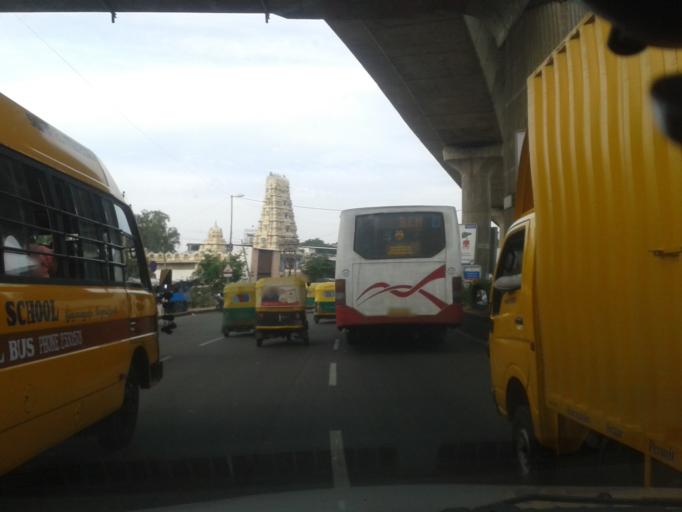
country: IN
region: Karnataka
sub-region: Bangalore Urban
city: Bangalore
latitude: 13.0111
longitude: 77.5504
